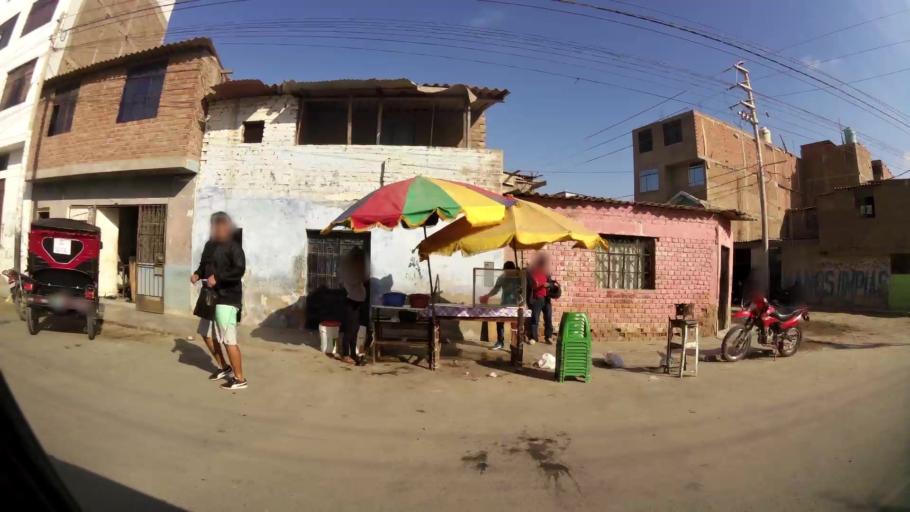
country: PE
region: Lambayeque
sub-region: Provincia de Chiclayo
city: Chiclayo
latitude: -6.7640
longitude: -79.8504
